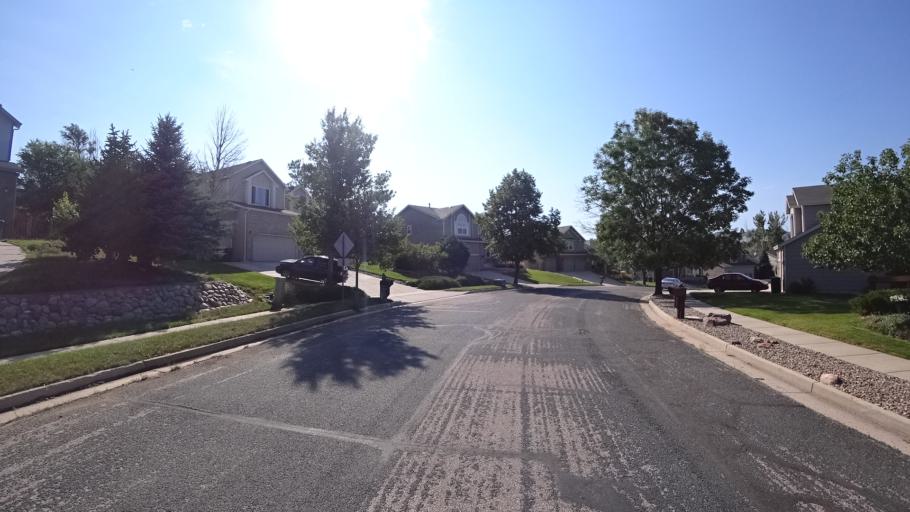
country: US
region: Colorado
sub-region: El Paso County
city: Air Force Academy
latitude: 38.9505
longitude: -104.7822
